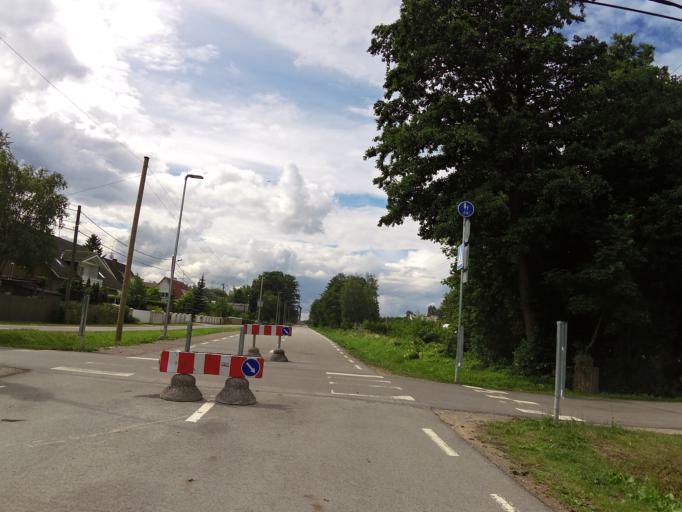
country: EE
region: Harju
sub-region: Tallinna linn
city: Tallinn
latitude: 59.4262
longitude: 24.6817
